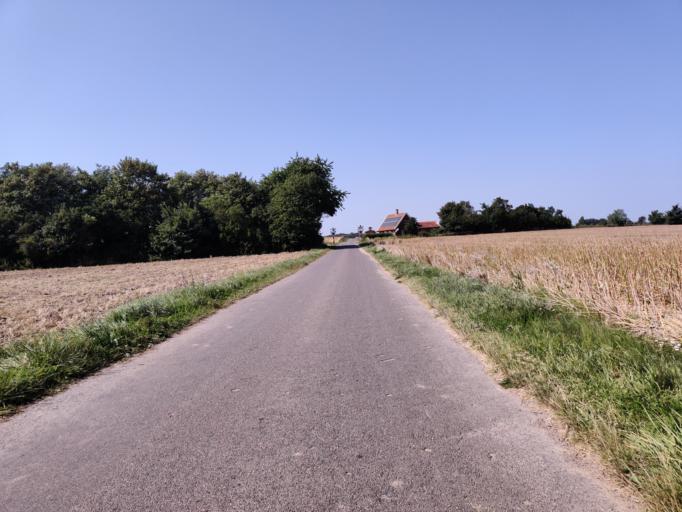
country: DK
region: Zealand
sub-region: Guldborgsund Kommune
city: Nykobing Falster
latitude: 54.6812
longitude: 11.9011
